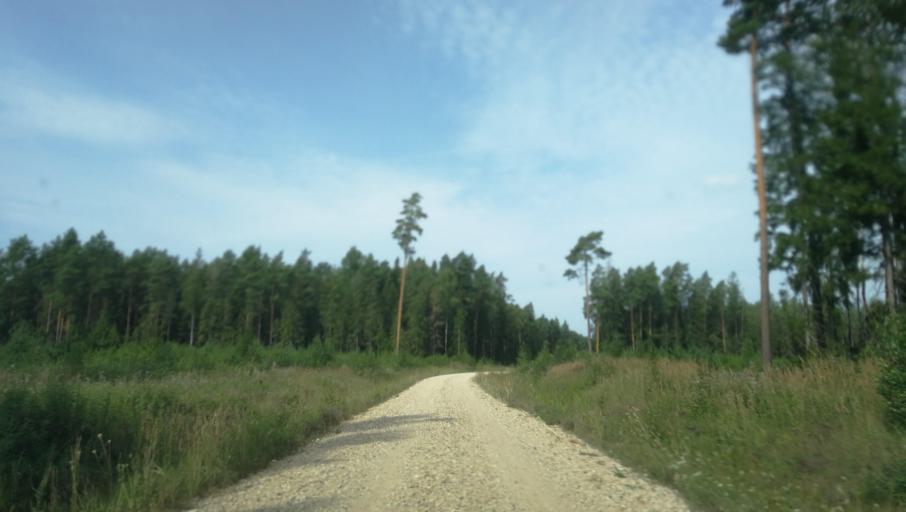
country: LV
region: Pavilostas
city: Pavilosta
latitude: 56.8150
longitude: 21.3342
